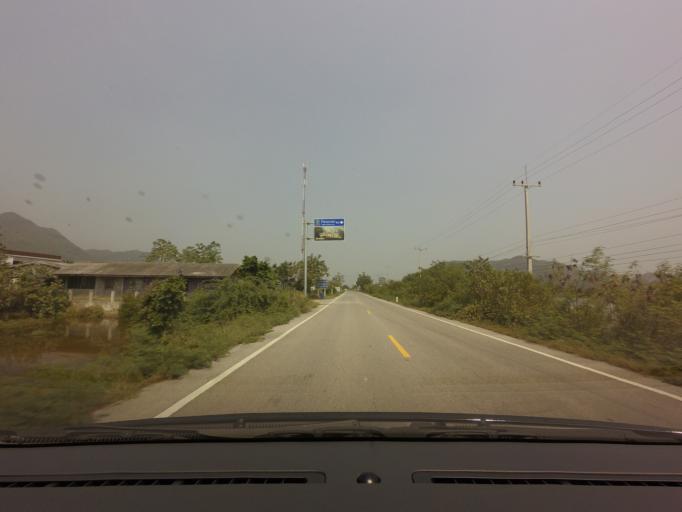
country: TH
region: Prachuap Khiri Khan
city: Sam Roi Yot
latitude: 12.1946
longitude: 99.9788
